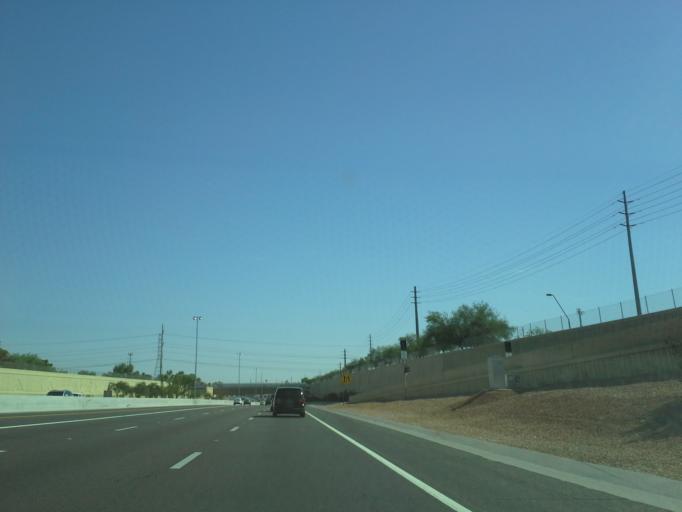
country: US
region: Arizona
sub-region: Maricopa County
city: San Carlos
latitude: 33.3609
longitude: -111.8943
